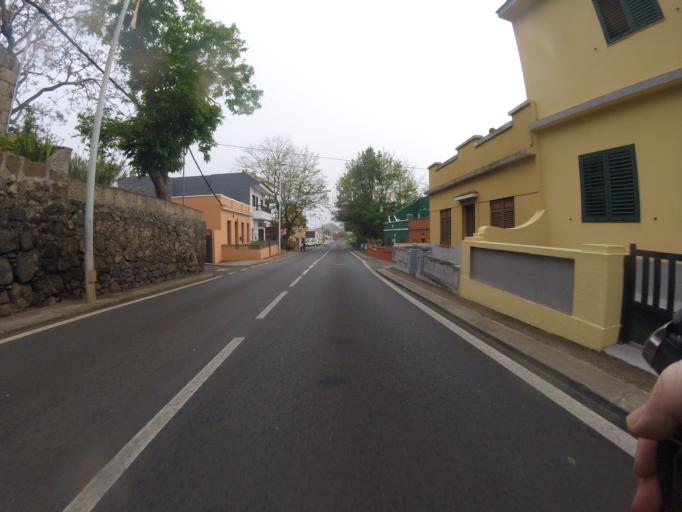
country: ES
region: Canary Islands
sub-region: Provincia de Santa Cruz de Tenerife
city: Tacoronte
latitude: 28.4926
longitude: -16.3756
